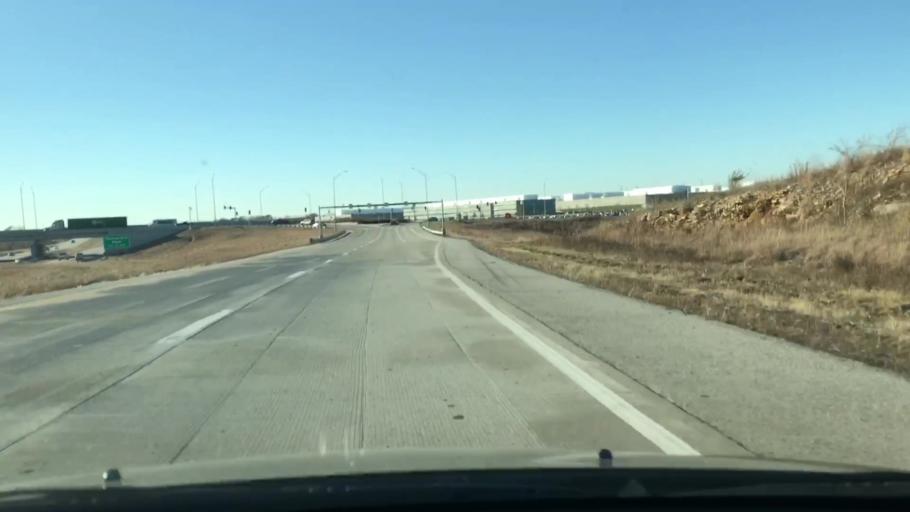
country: US
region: Missouri
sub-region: Jackson County
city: Grandview
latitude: 38.8588
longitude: -94.5435
